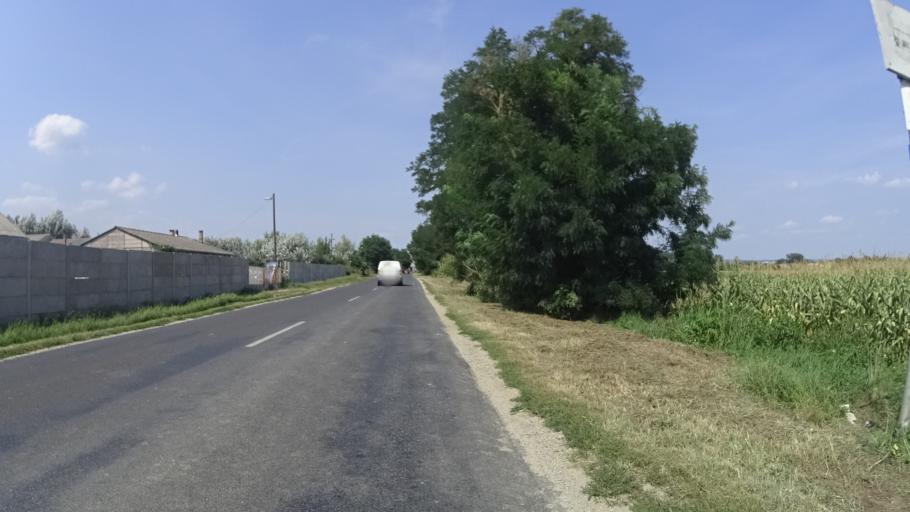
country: HU
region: Zala
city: Nagykanizsa
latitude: 46.4419
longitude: 16.9546
